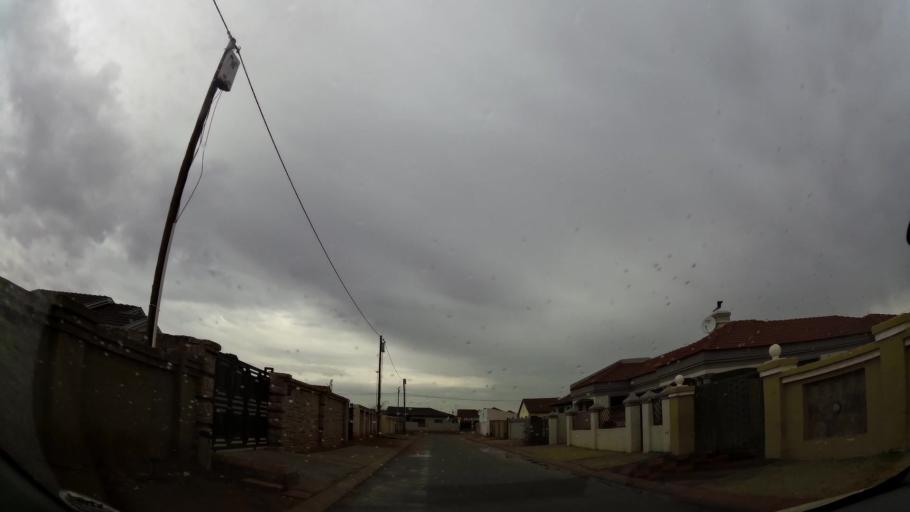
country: ZA
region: Gauteng
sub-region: Ekurhuleni Metropolitan Municipality
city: Germiston
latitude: -26.3345
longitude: 28.2071
